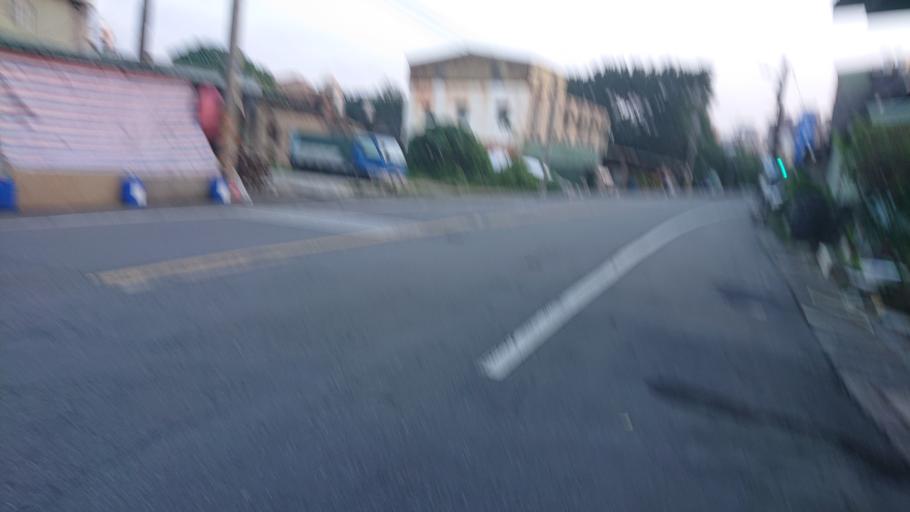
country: TW
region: Taipei
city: Taipei
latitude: 25.1881
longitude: 121.4199
